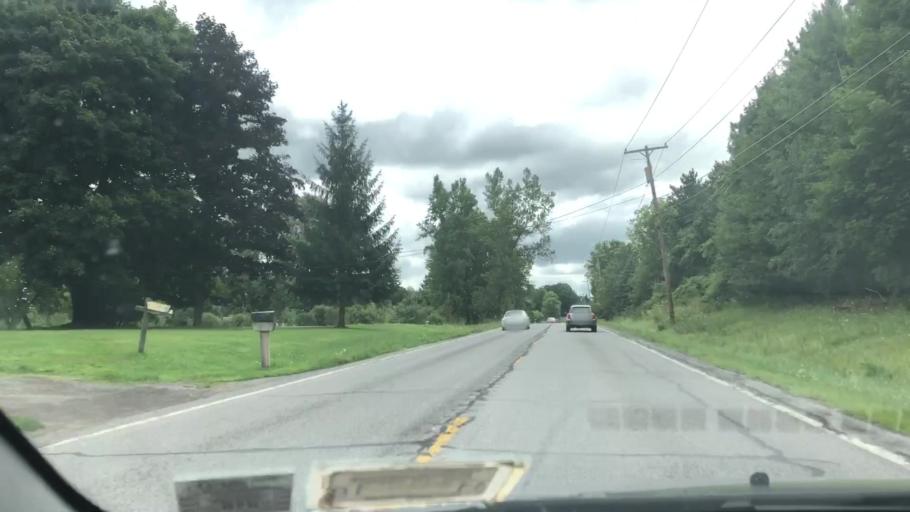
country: US
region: New York
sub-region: Wayne County
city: Macedon
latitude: 43.1270
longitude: -77.2927
